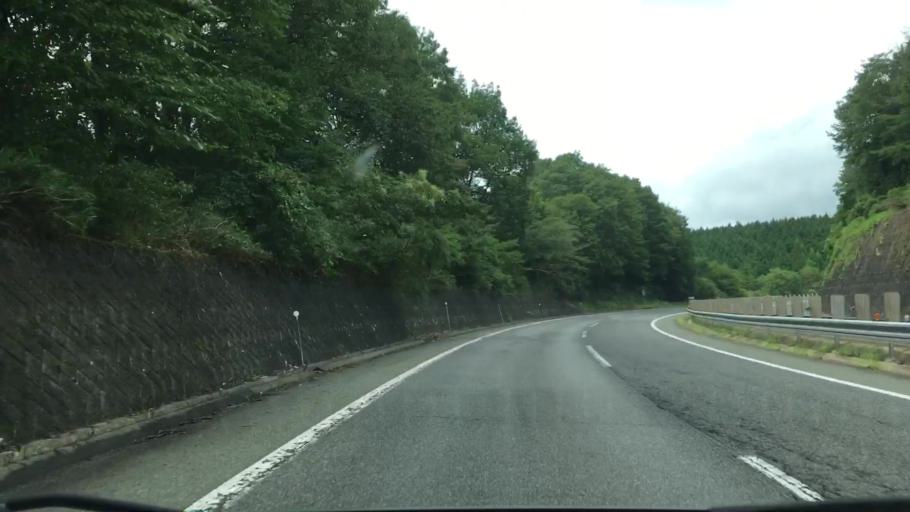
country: JP
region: Hiroshima
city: Shobara
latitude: 34.8924
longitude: 133.2160
